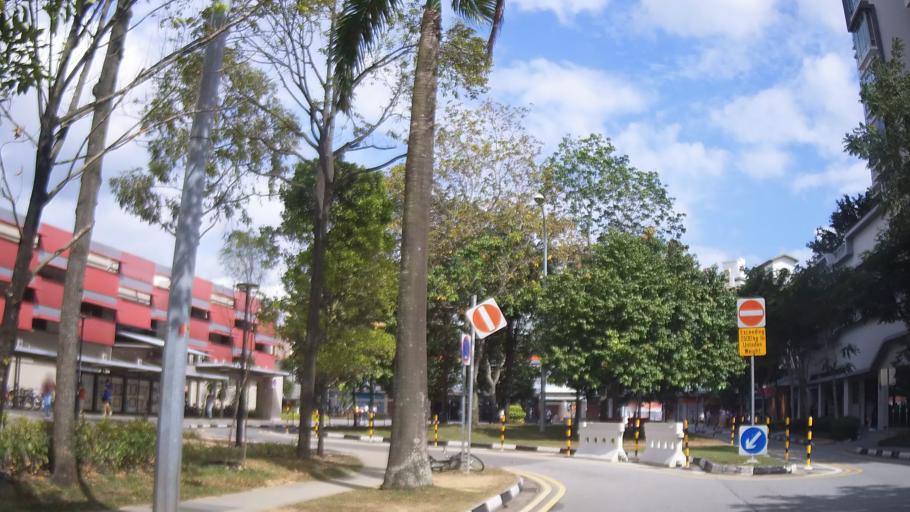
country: MY
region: Johor
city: Johor Bahru
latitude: 1.3977
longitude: 103.7463
